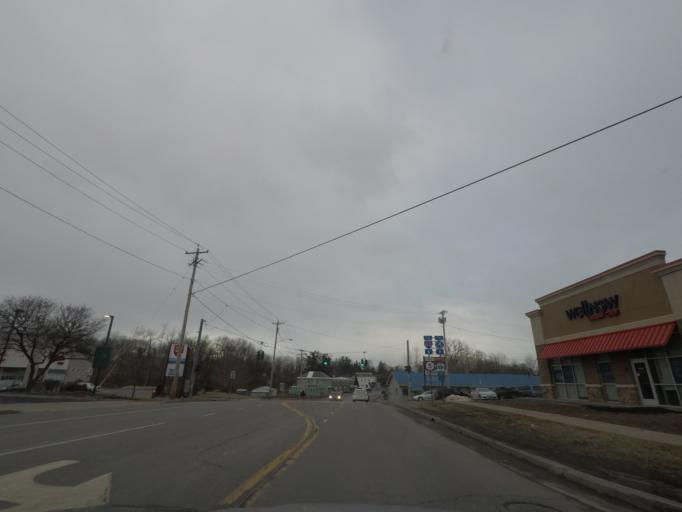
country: US
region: New York
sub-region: Madison County
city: Oneida
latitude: 43.0789
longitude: -75.6418
